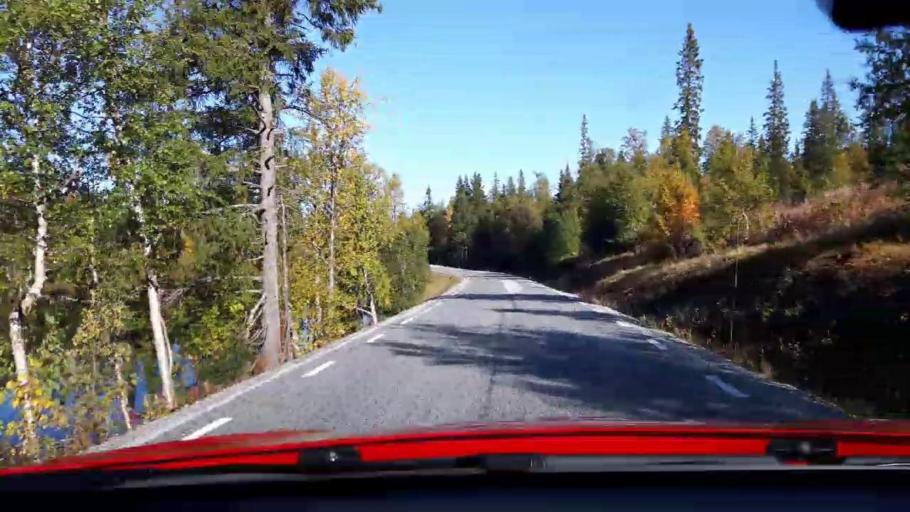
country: NO
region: Nord-Trondelag
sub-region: Lierne
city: Sandvika
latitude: 64.6138
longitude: 13.7016
